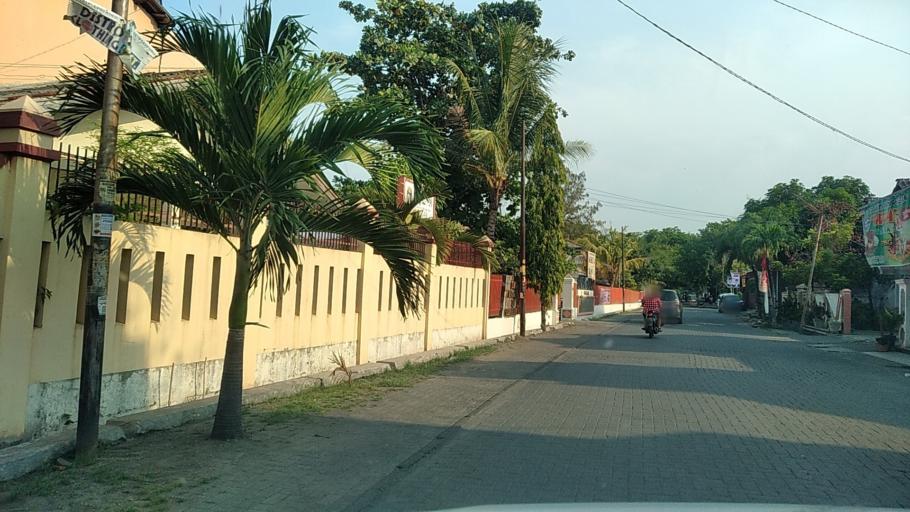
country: ID
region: Central Java
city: Semarang
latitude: -6.9640
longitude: 110.4057
